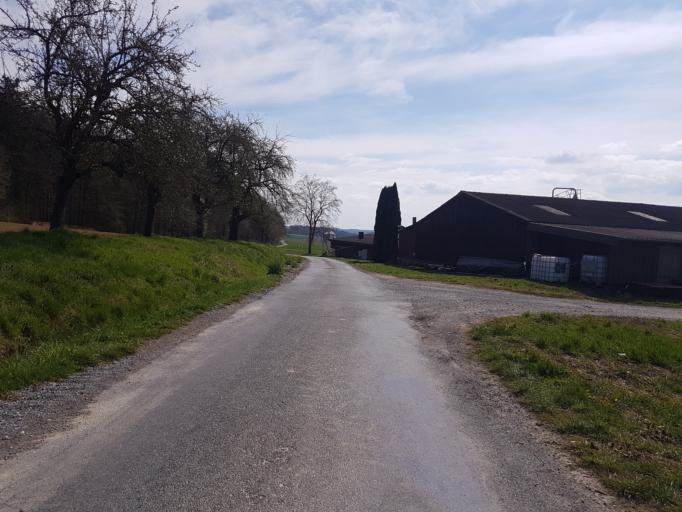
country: DE
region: Baden-Wuerttemberg
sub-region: Regierungsbezirk Stuttgart
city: Jagsthausen
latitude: 49.3782
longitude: 9.5174
